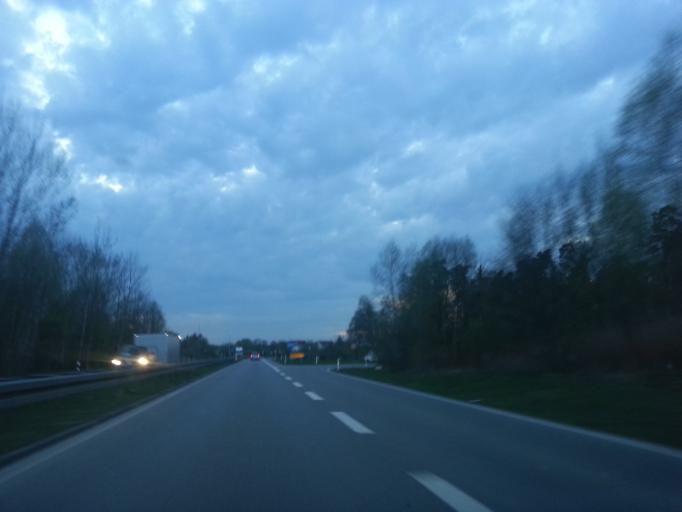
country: DE
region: Baden-Wuerttemberg
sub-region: Tuebingen Region
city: Eriskirch
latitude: 47.6275
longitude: 9.5467
